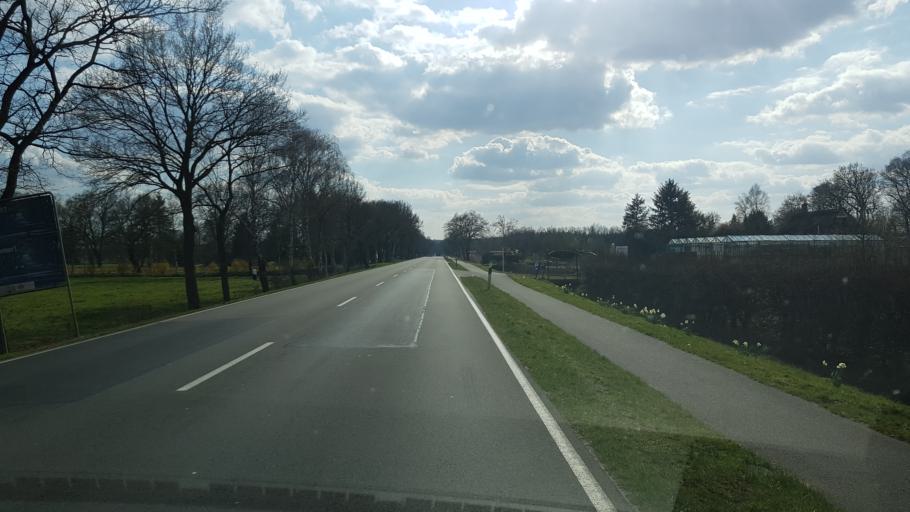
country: DE
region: Lower Saxony
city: Rastede
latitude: 53.2441
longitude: 8.2909
